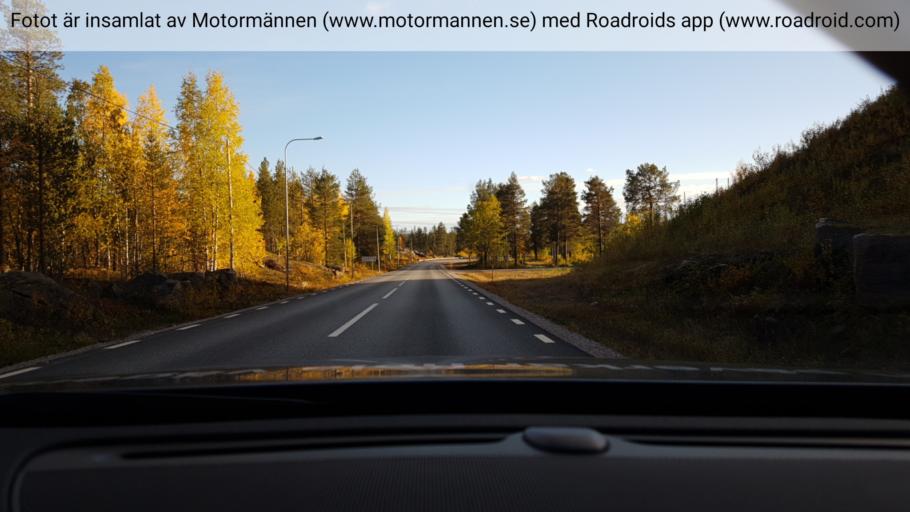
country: SE
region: Norrbotten
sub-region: Jokkmokks Kommun
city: Jokkmokk
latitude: 66.8857
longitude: 19.8294
